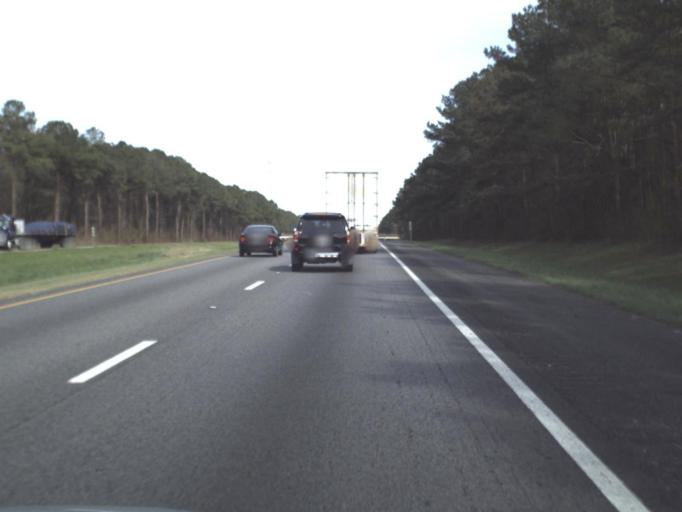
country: US
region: Florida
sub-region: Leon County
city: Tallahassee
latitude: 30.4780
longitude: -84.0974
